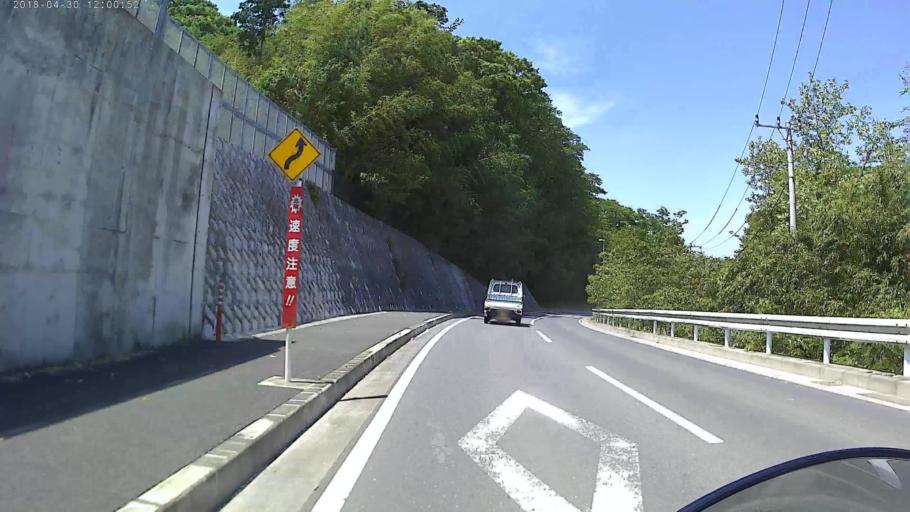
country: JP
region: Kanagawa
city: Zama
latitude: 35.5132
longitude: 139.3271
